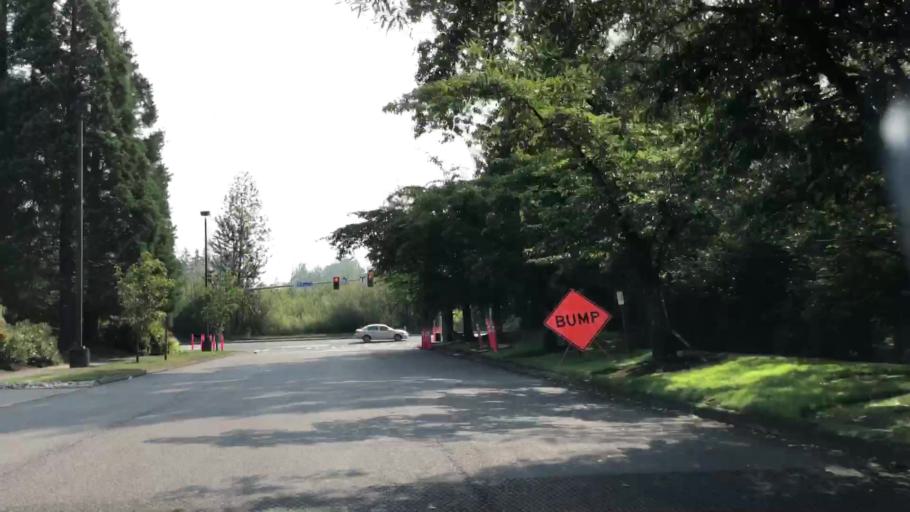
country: US
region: Washington
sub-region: Snohomish County
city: Alderwood Manor
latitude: 47.8106
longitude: -122.2935
